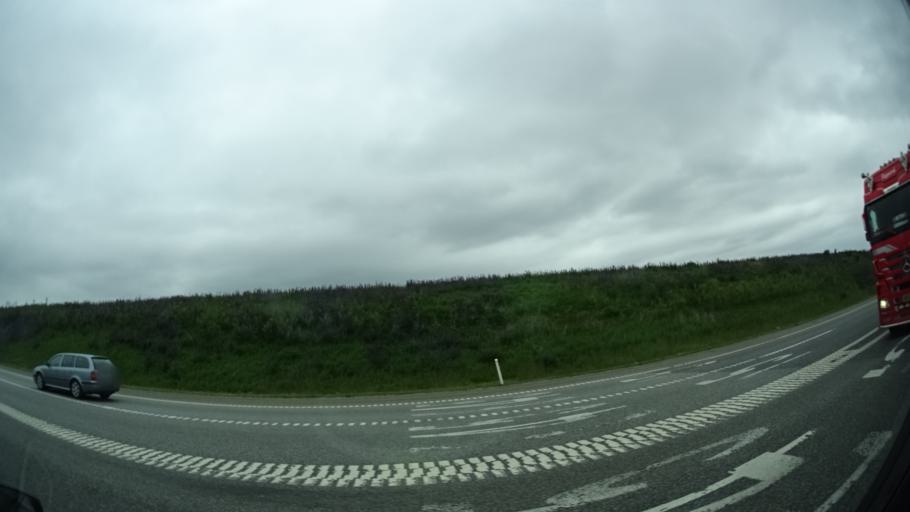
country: DK
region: Central Jutland
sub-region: Arhus Kommune
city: Trige
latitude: 56.2124
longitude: 10.1502
